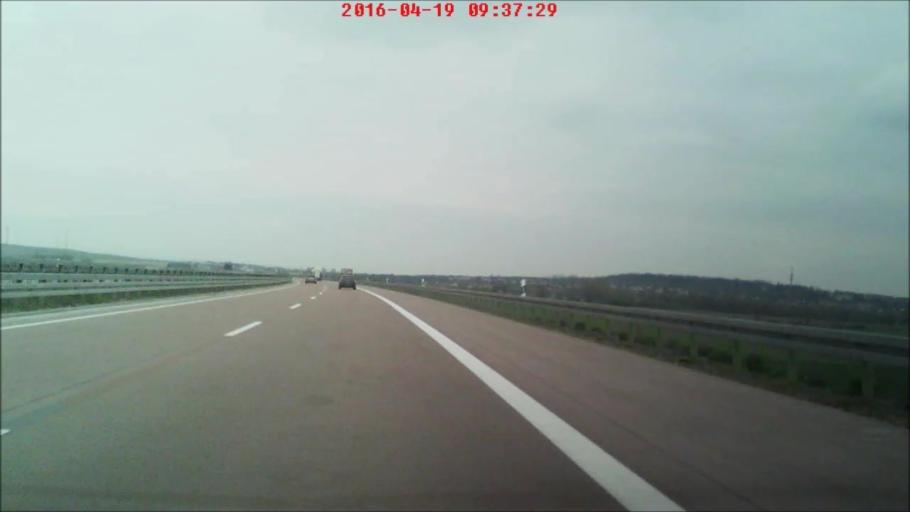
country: DE
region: Thuringia
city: Reinsdorf
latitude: 51.3502
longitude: 11.2670
